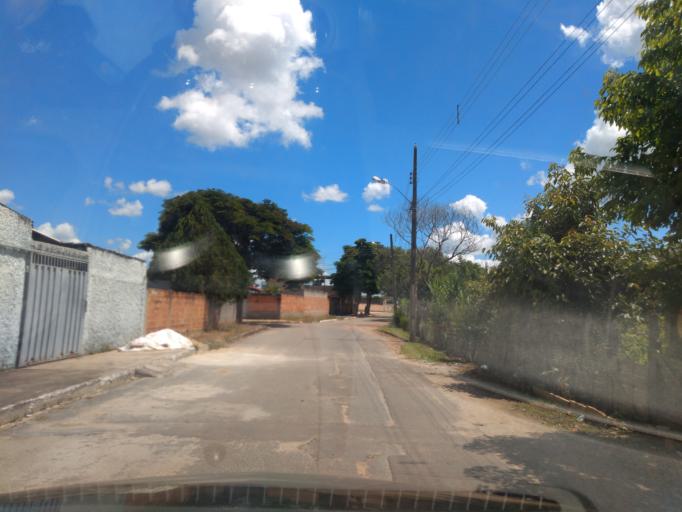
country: BR
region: Minas Gerais
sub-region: Tres Coracoes
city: Tres Coracoes
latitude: -21.6778
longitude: -45.2449
